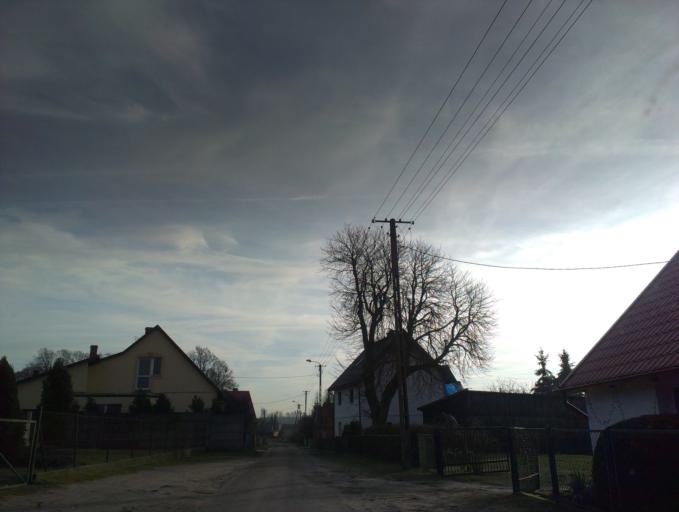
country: PL
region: Pomeranian Voivodeship
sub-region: Powiat czluchowski
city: Debrzno
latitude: 53.6164
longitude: 17.1860
